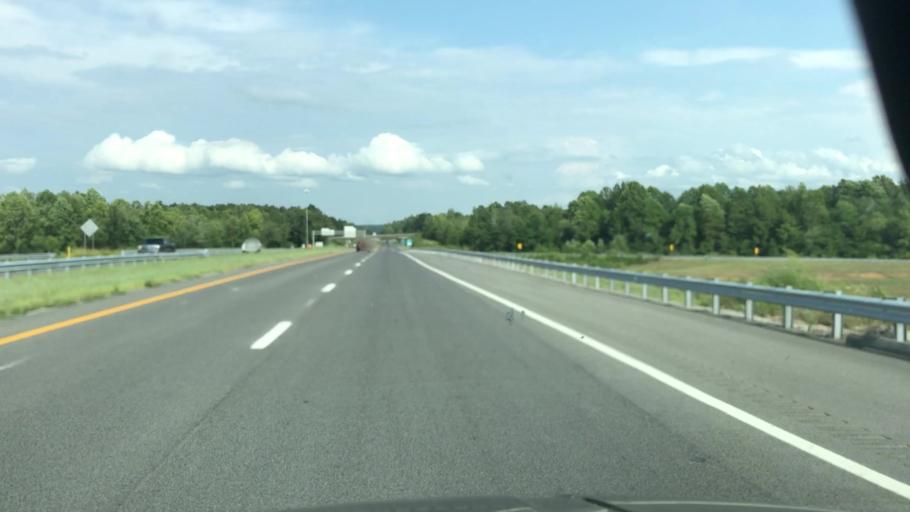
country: US
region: Kentucky
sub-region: Hopkins County
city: Nortonville
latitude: 37.2123
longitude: -87.4406
